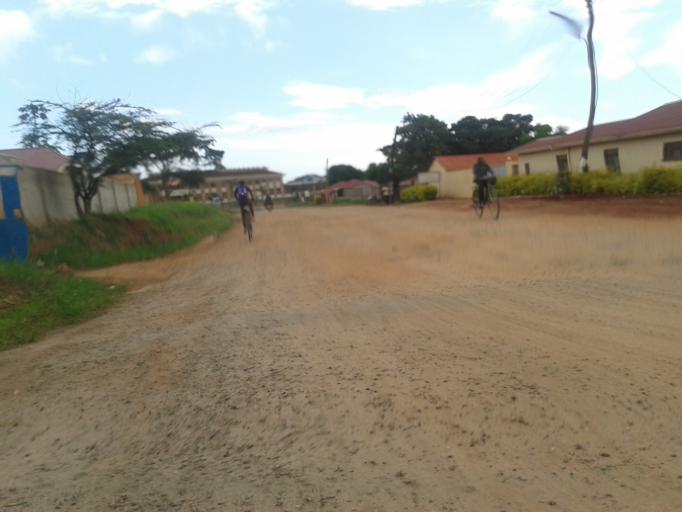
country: UG
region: Northern Region
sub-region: Gulu District
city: Gulu
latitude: 2.7785
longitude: 32.2953
